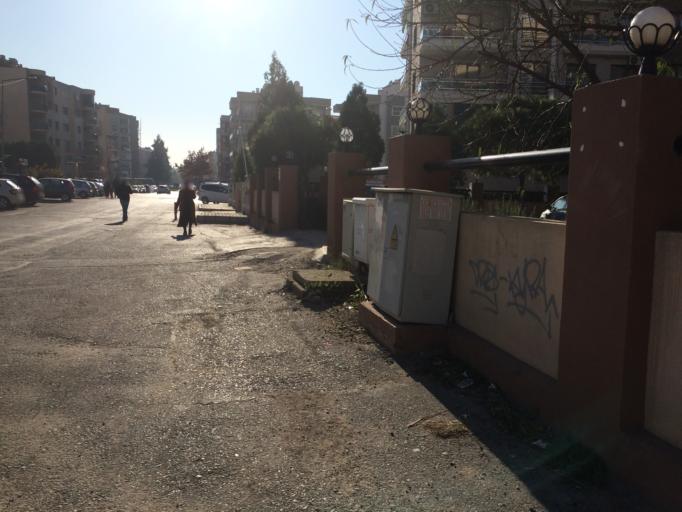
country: TR
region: Izmir
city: Karsiyaka
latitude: 38.4874
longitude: 27.0582
